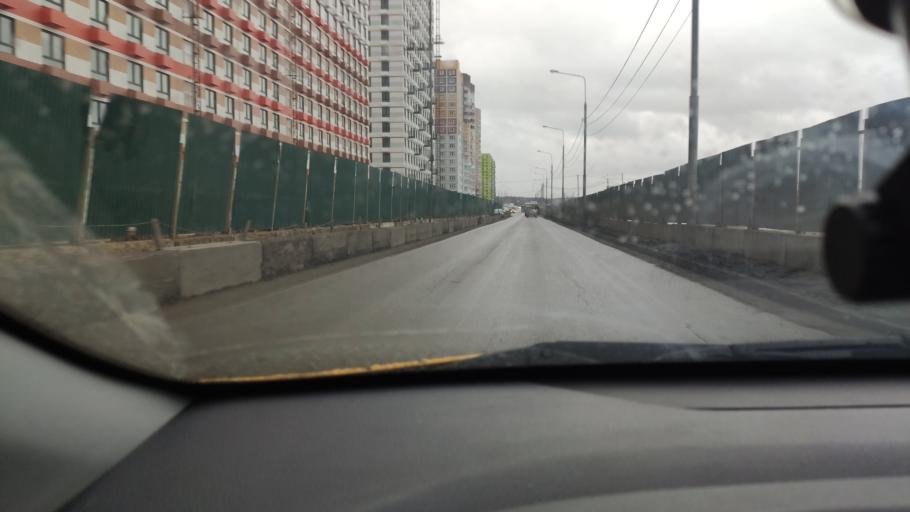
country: RU
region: Moscow
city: Annino
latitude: 55.5367
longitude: 37.6133
